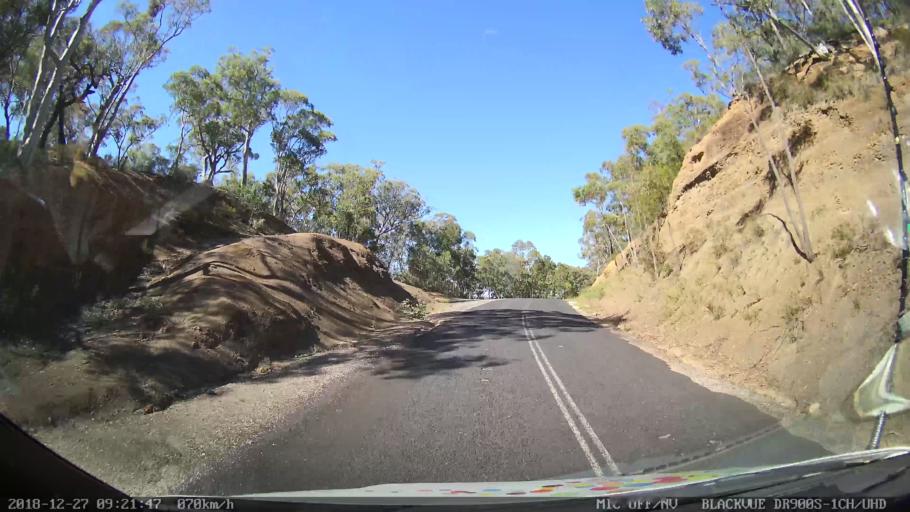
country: AU
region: New South Wales
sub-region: Lithgow
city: Portland
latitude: -33.1275
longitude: 150.0149
